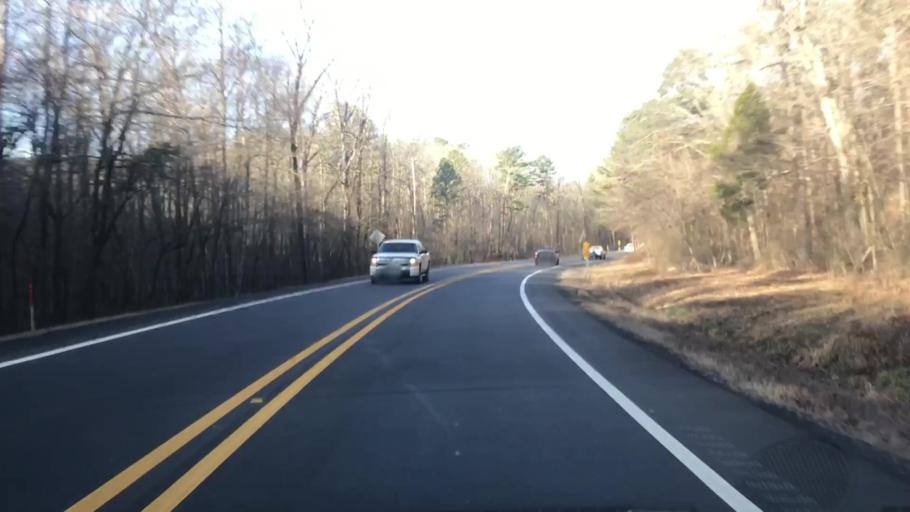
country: US
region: Arkansas
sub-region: Montgomery County
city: Mount Ida
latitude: 34.5234
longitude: -93.4103
